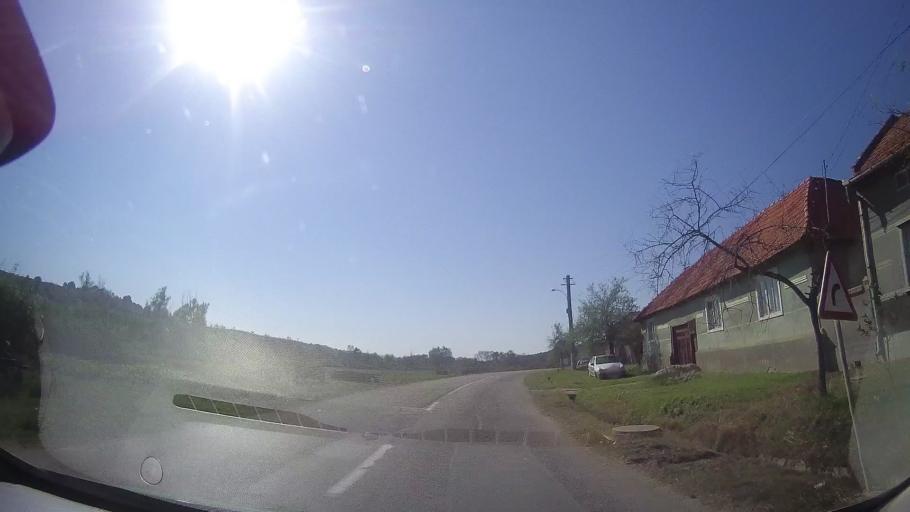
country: RO
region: Timis
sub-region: Comuna Ohaba Lunga
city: Ohaba Lunga
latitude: 45.9032
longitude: 21.9797
